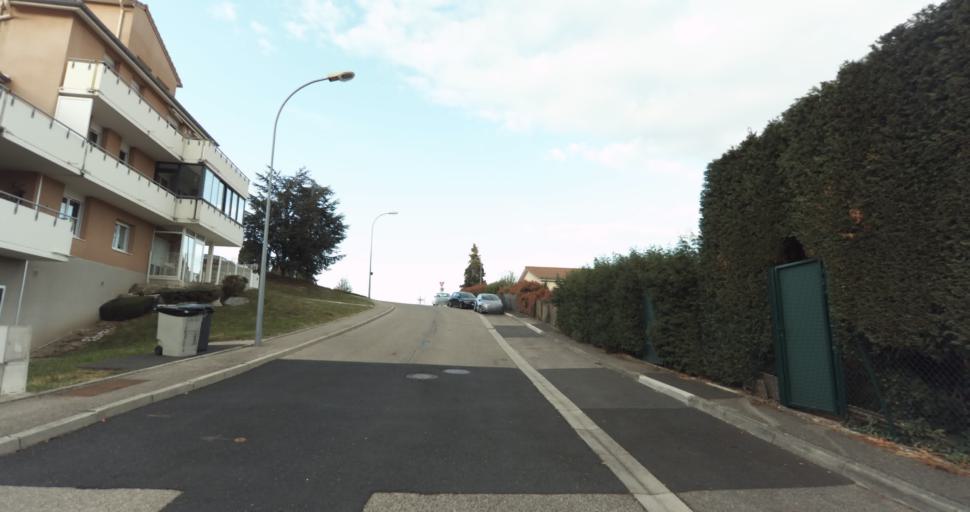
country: FR
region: Rhone-Alpes
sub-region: Departement de la Loire
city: Saint-Jean-Bonnefonds
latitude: 45.4493
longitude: 4.4469
